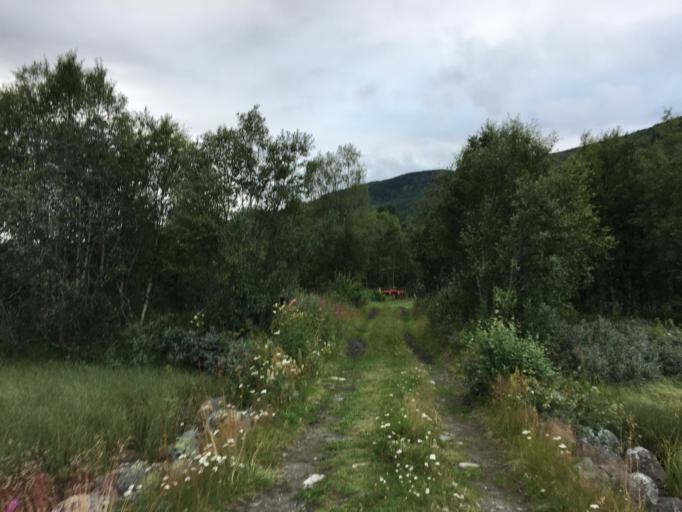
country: NO
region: Buskerud
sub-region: Hol
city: Hol
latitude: 60.6179
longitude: 8.2241
